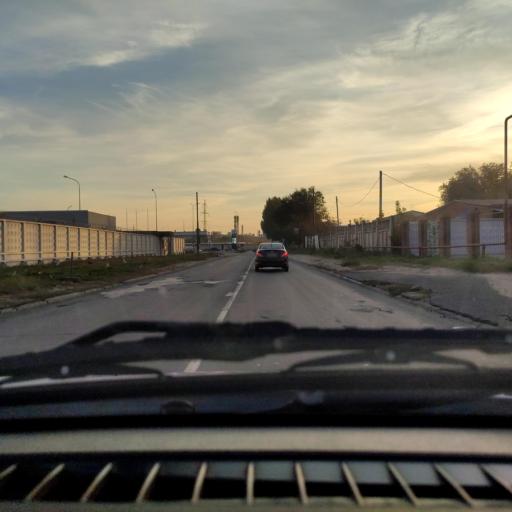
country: RU
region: Samara
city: Tol'yatti
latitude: 53.5352
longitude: 49.4324
